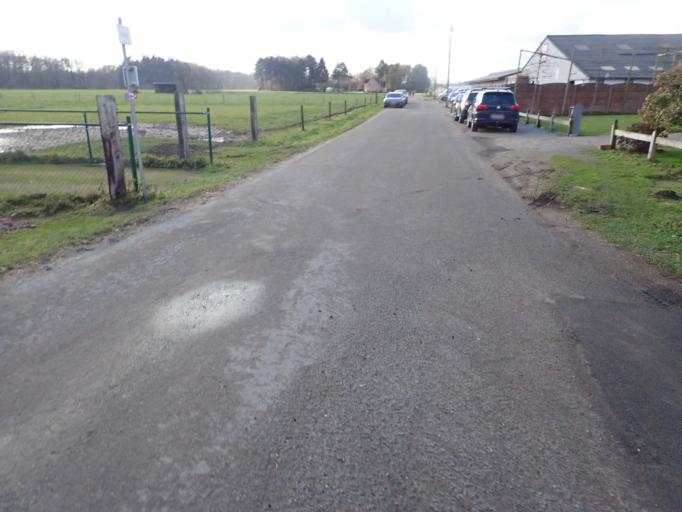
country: BE
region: Flanders
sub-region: Provincie Antwerpen
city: Grobbendonk
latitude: 51.2261
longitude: 4.7179
